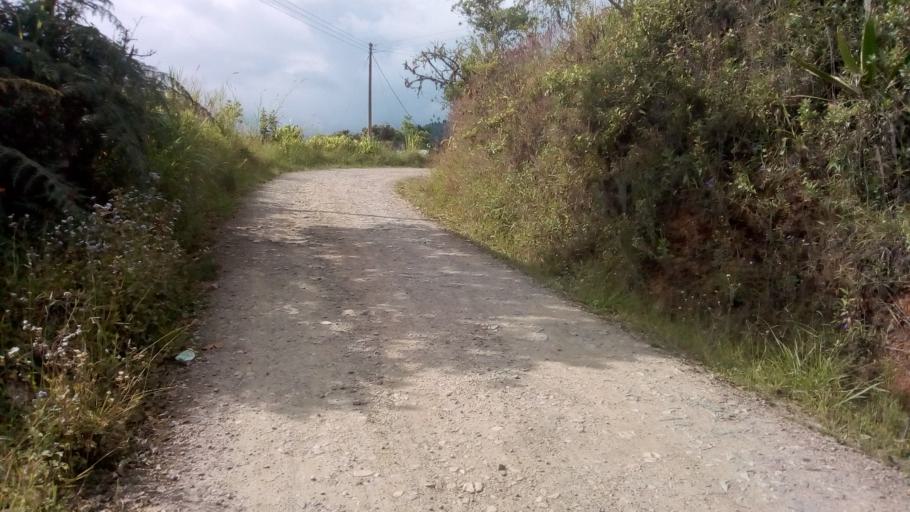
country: CO
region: Cundinamarca
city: Tenza
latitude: 5.0960
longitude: -73.4206
